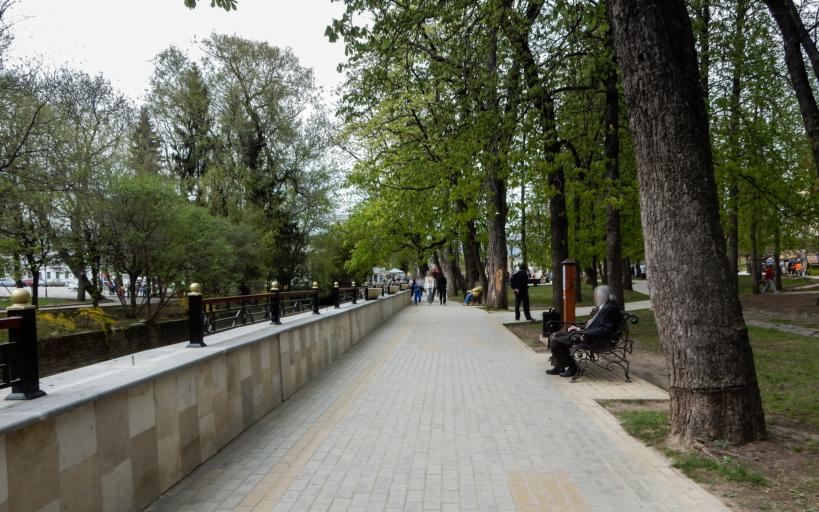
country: RU
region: Stavropol'skiy
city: Kislovodsk
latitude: 43.8977
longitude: 42.7176
